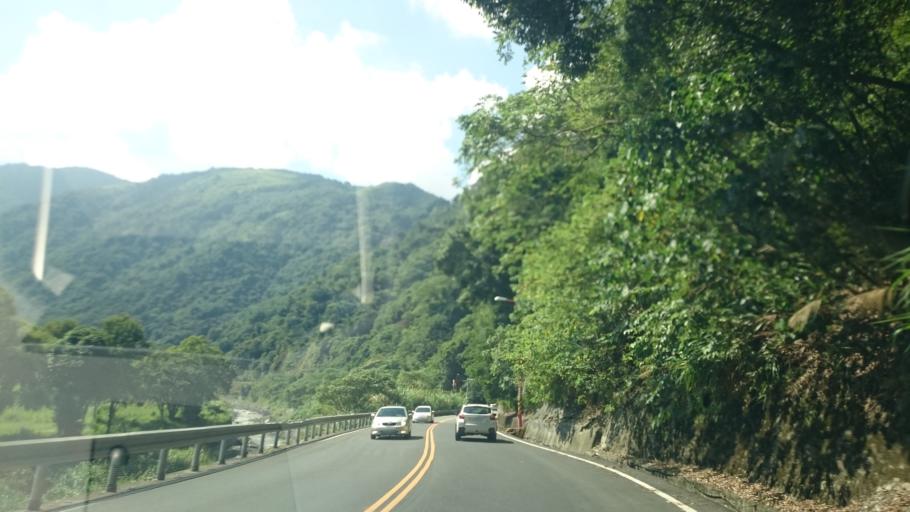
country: TW
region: Taiwan
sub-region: Nantou
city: Puli
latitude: 24.0012
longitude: 121.0665
